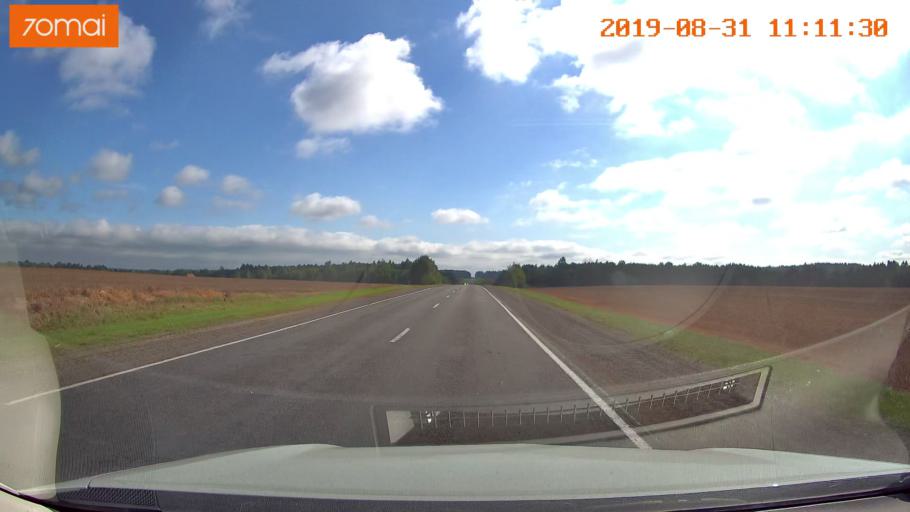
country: BY
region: Mogilev
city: Ramanavichy
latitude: 53.8182
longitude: 30.7558
